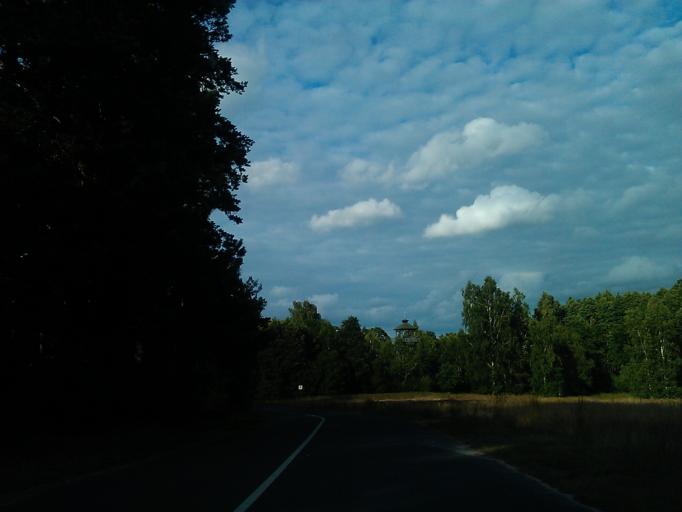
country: LV
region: Stopini
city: Ulbroka
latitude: 56.9645
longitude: 24.2852
